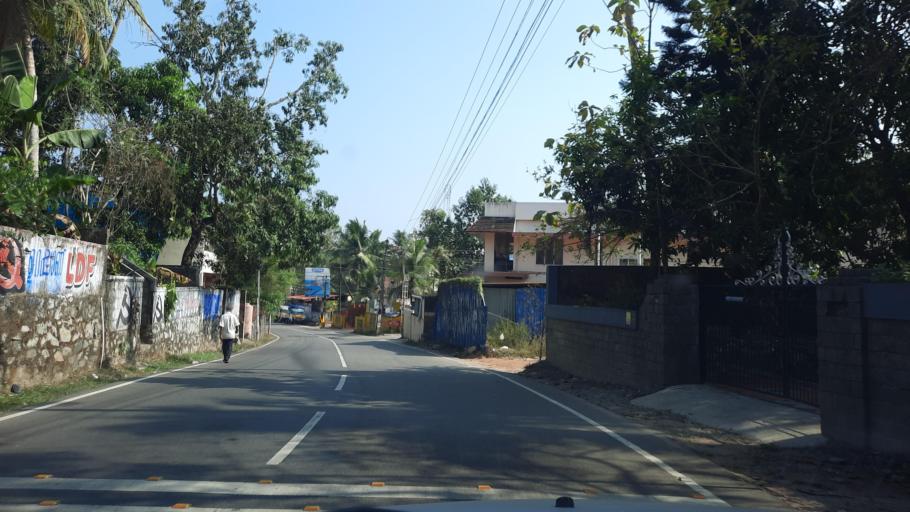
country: IN
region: Kerala
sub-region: Thiruvananthapuram
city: Thiruvananthapuram
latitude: 8.5602
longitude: 76.9216
